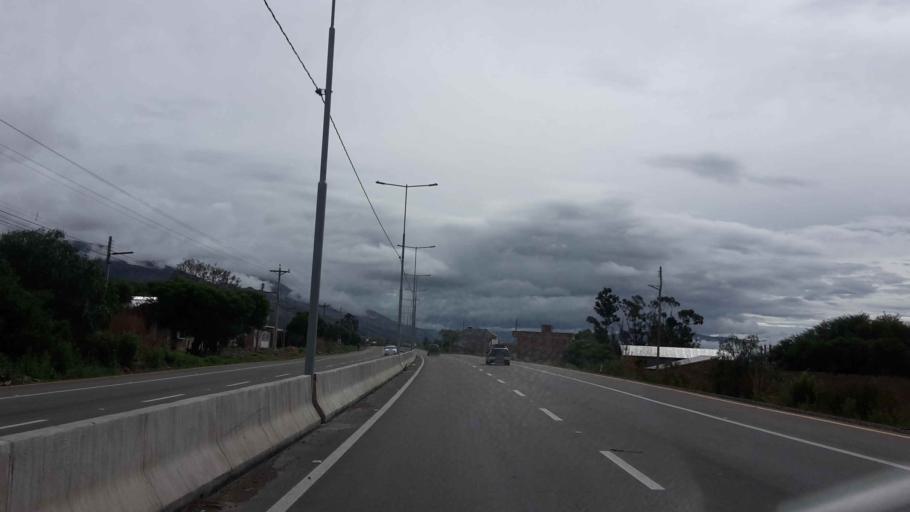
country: BO
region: Cochabamba
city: Tarata
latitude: -17.5420
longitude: -65.9959
